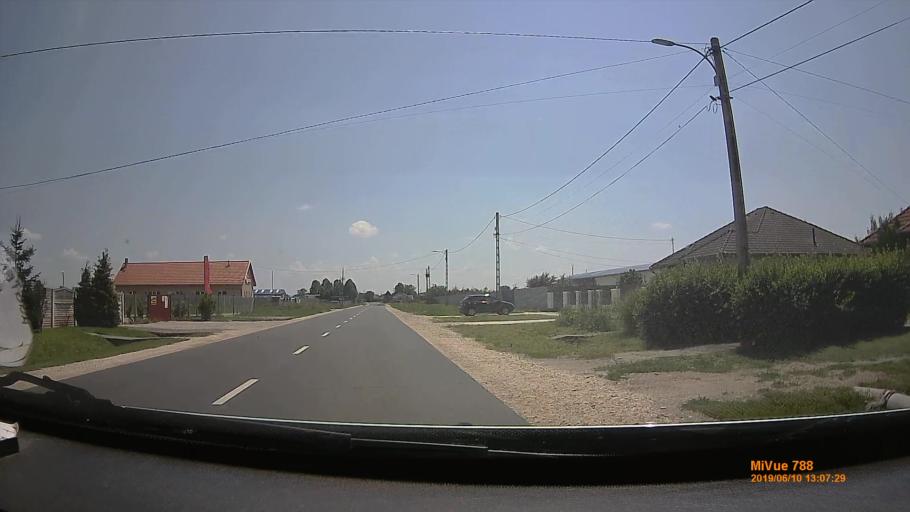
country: HU
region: Borsod-Abauj-Zemplen
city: Gesztely
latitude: 48.0869
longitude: 20.9688
